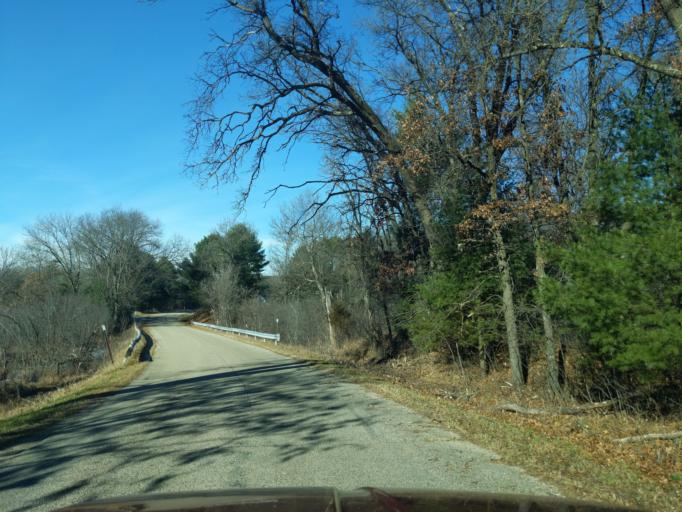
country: US
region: Wisconsin
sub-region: Waushara County
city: Silver Lake
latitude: 44.1115
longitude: -89.1702
